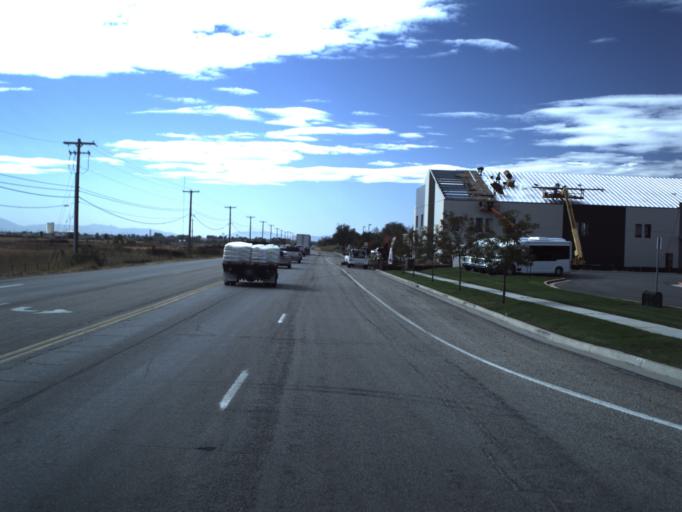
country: US
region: Utah
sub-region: Davis County
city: North Salt Lake
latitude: 40.8301
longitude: -111.9372
